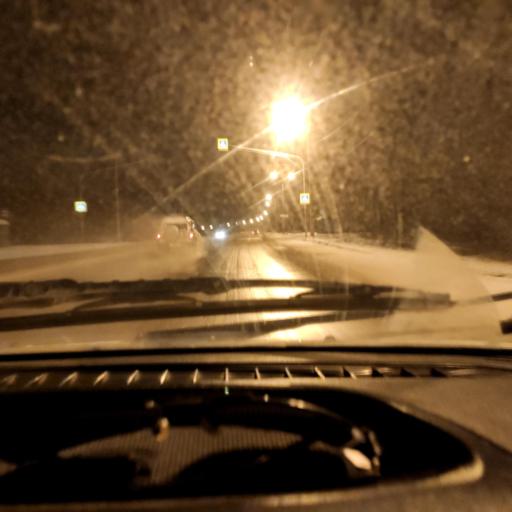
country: RU
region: Samara
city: Zhigulevsk
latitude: 53.4966
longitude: 49.5075
